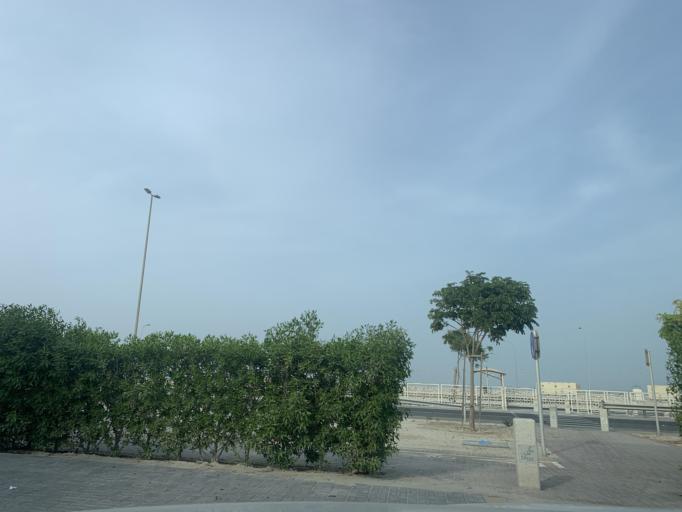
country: BH
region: Muharraq
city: Al Muharraq
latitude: 26.3170
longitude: 50.6312
